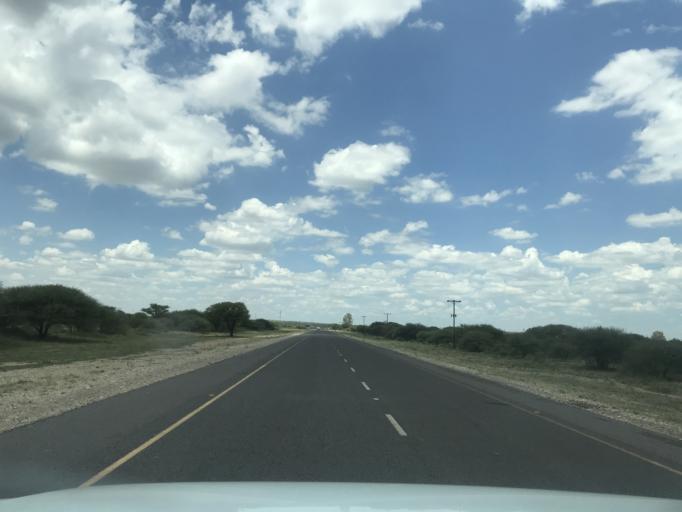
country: BW
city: Mabuli
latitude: -25.7301
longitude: 25.1114
